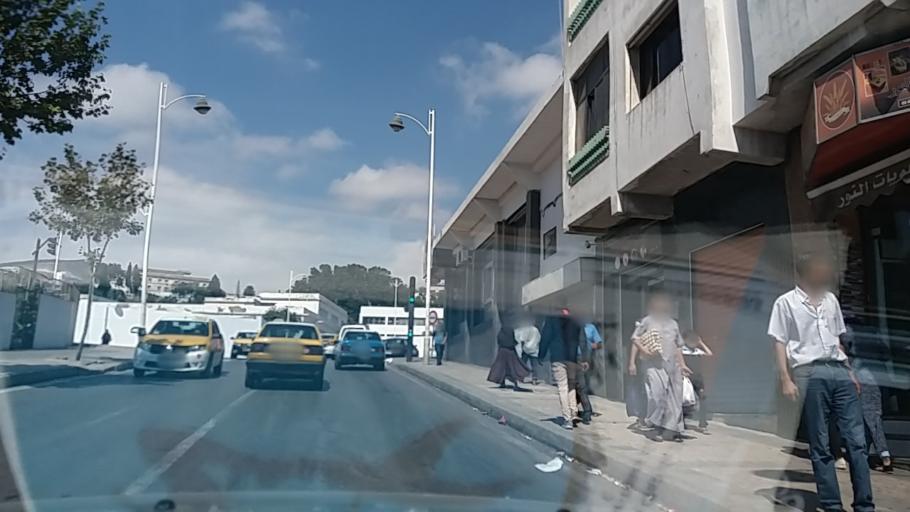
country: MA
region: Tanger-Tetouan
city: Tetouan
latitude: 35.5651
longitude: -5.3686
